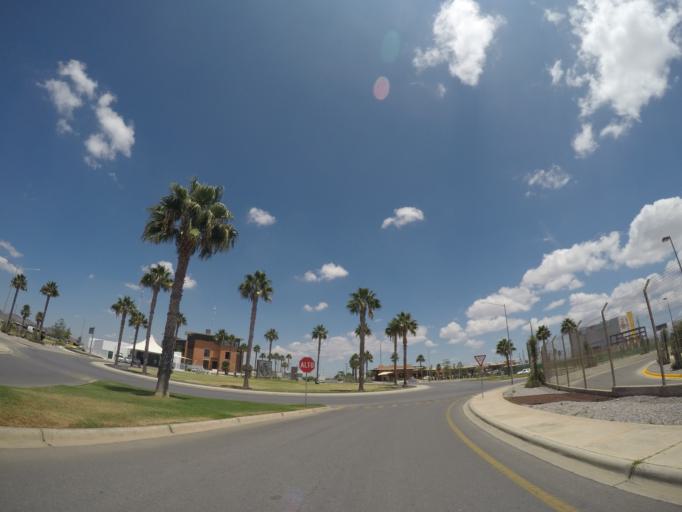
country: MX
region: San Luis Potosi
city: La Pila
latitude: 22.0401
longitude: -100.8940
